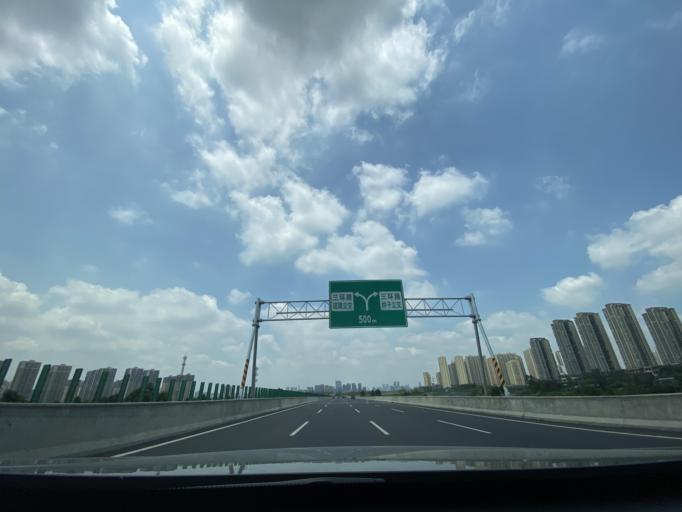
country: CN
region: Sichuan
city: Chengdu
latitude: 30.5928
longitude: 104.1219
